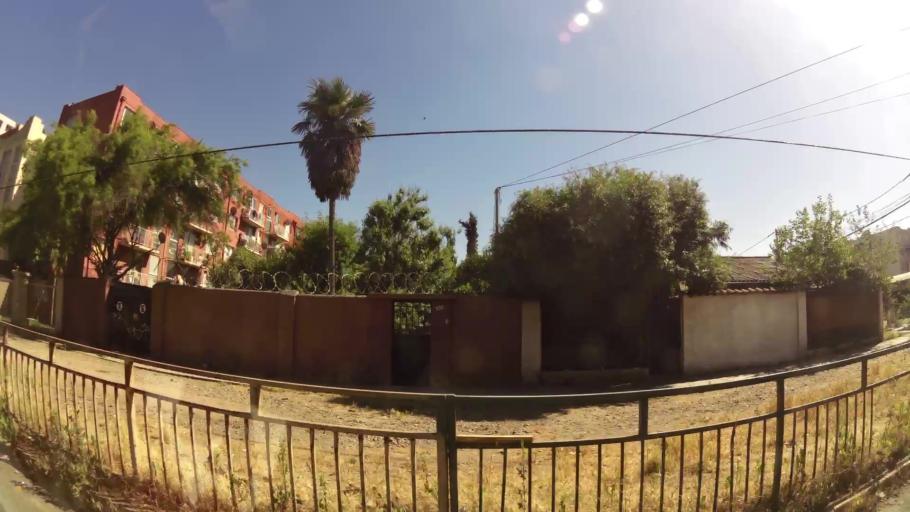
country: CL
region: Santiago Metropolitan
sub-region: Provincia de Santiago
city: La Pintana
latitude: -33.5412
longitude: -70.6593
